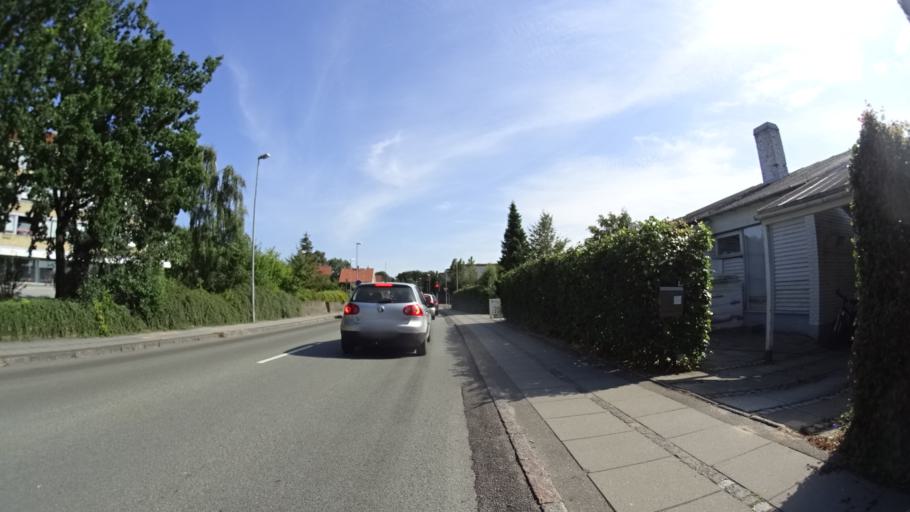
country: DK
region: Central Jutland
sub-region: Arhus Kommune
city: Stavtrup
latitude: 56.1177
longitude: 10.1726
